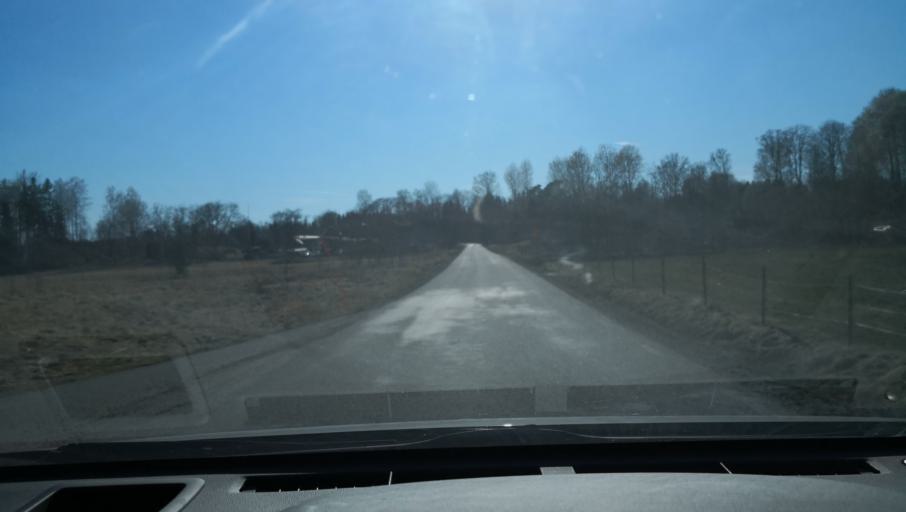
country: SE
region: Dalarna
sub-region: Avesta Kommun
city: Avesta
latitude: 60.0718
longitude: 16.3763
